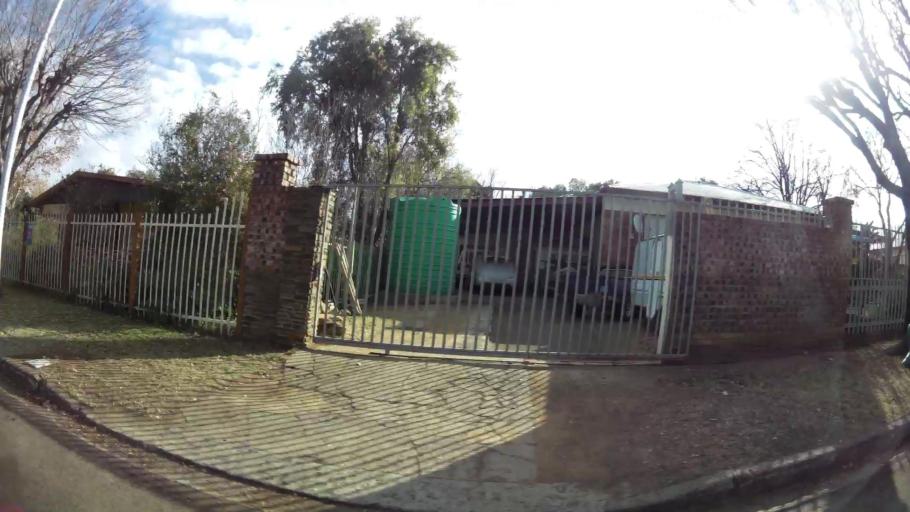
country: ZA
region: Orange Free State
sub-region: Mangaung Metropolitan Municipality
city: Bloemfontein
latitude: -29.0794
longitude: 26.2140
